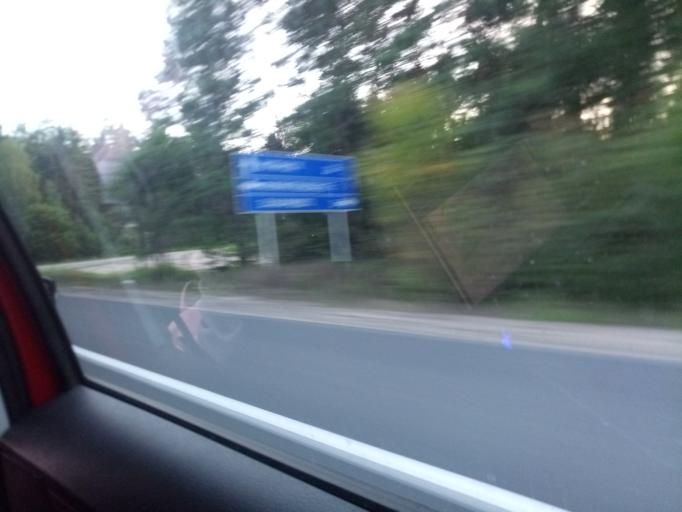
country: RU
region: Moskovskaya
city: Noginsk-9
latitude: 56.1025
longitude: 38.5853
